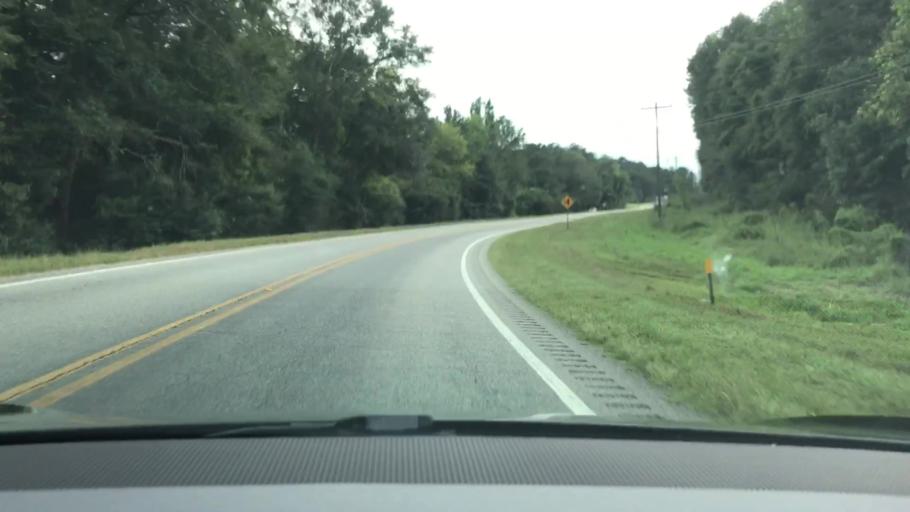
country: US
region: Alabama
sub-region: Coffee County
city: Elba
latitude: 31.5774
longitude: -85.9976
